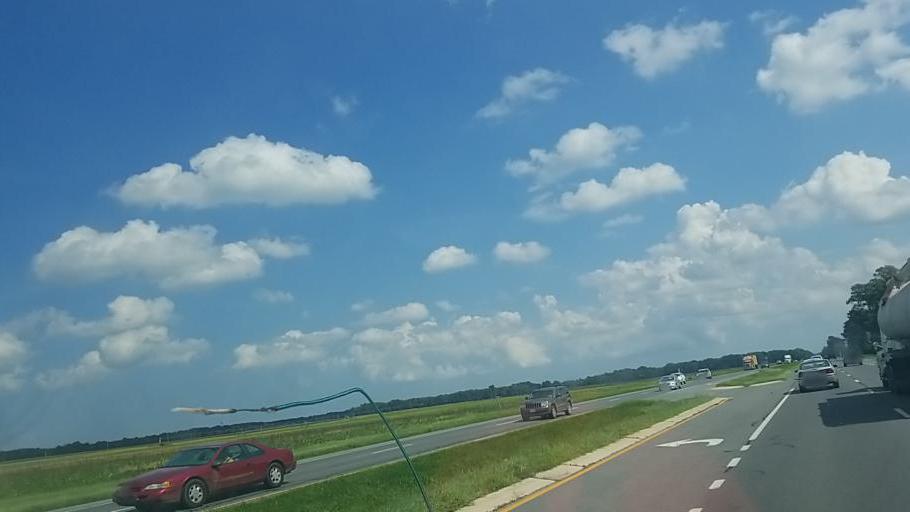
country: US
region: Delaware
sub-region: Sussex County
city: Millsboro
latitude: 38.6261
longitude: -75.3428
